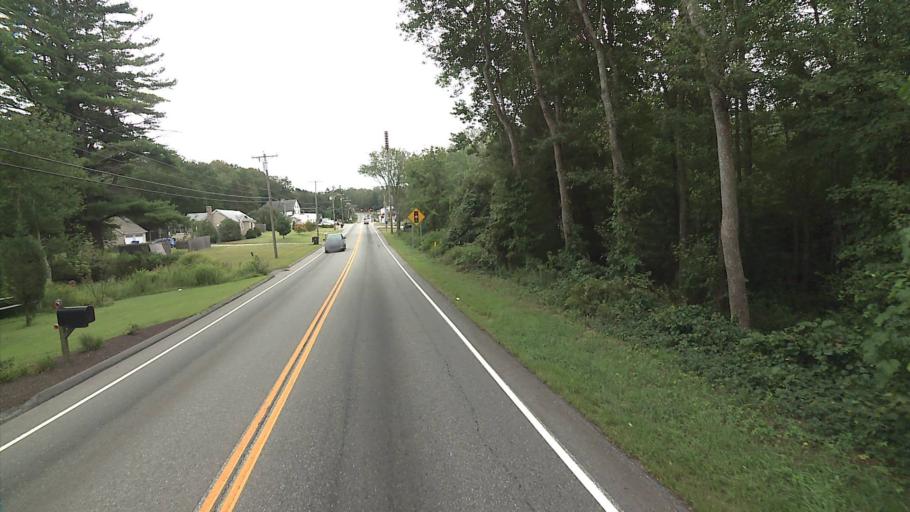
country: US
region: Connecticut
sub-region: New London County
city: Montville Center
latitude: 41.4306
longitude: -72.2190
